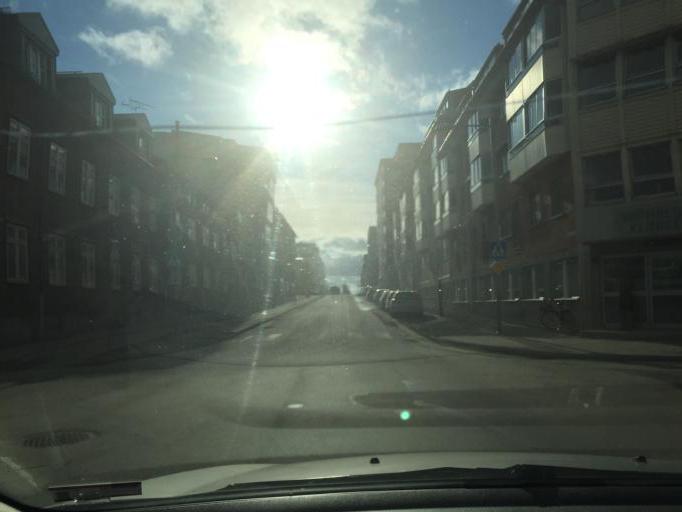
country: SE
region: Norrbotten
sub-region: Lulea Kommun
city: Lulea
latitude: 65.5859
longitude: 22.1592
